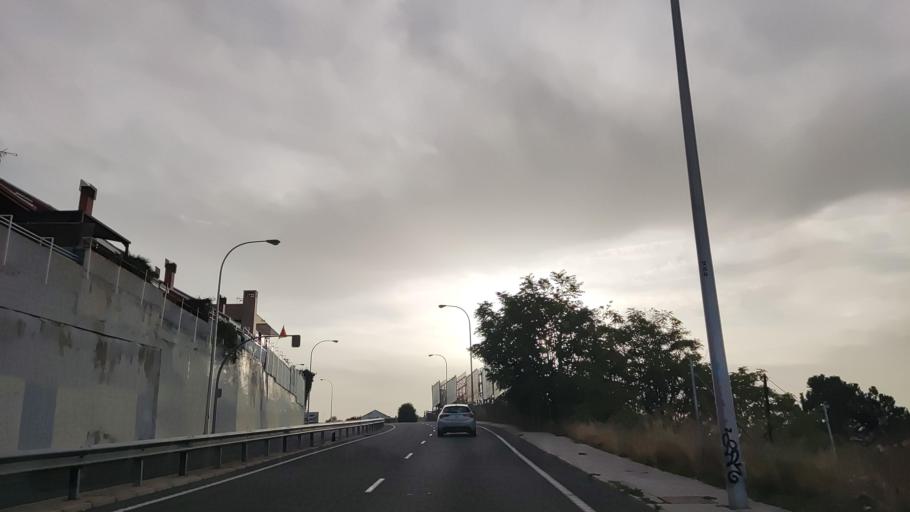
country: ES
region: Madrid
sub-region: Provincia de Madrid
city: Tetuan de las Victorias
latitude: 40.4769
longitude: -3.7348
